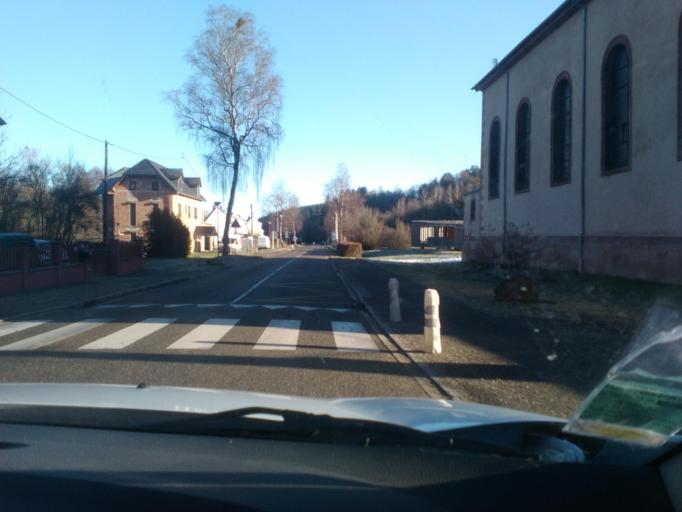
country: FR
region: Alsace
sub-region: Departement du Bas-Rhin
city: Rothau
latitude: 48.3590
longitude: 7.1351
